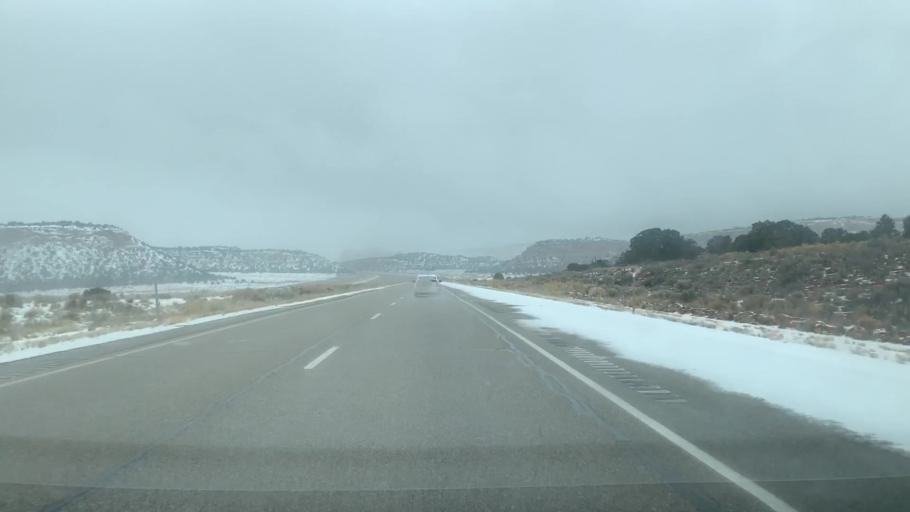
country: US
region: Utah
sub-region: Emery County
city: Castle Dale
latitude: 38.8712
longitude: -110.7266
